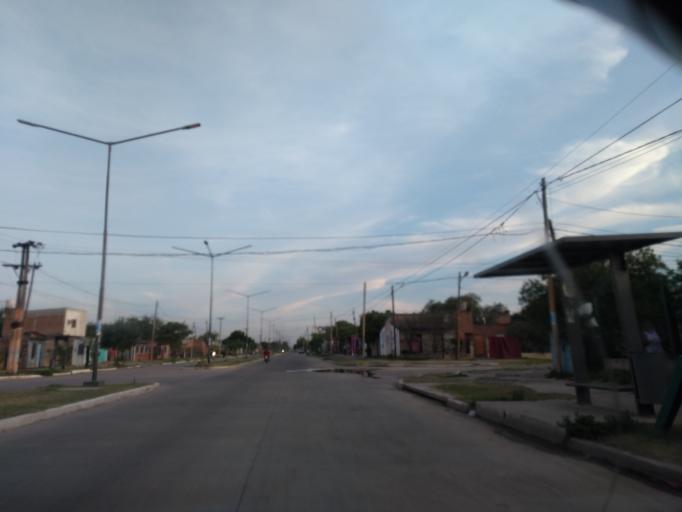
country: AR
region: Chaco
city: Resistencia
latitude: -27.4779
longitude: -58.9855
